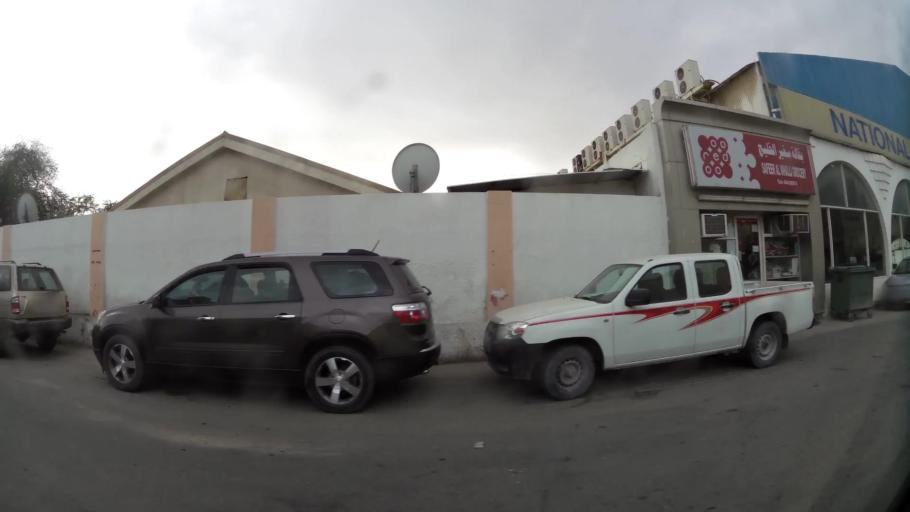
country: QA
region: Baladiyat ad Dawhah
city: Doha
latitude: 25.2720
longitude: 51.5072
